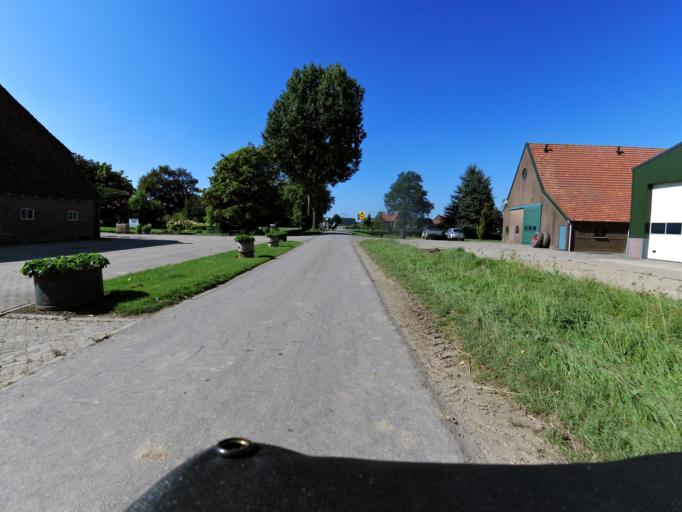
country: NL
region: South Holland
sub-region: Gemeente Dordrecht
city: Dordrecht
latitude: 51.7665
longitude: 4.7144
